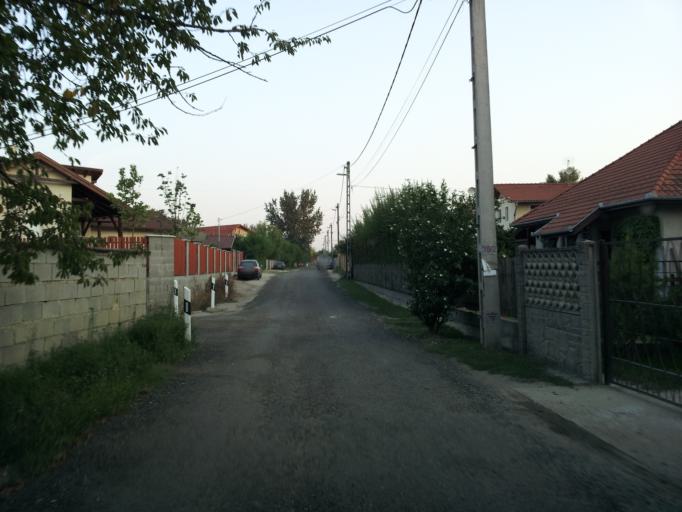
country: HU
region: Pest
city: Szigetszentmiklos
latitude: 47.3331
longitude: 19.0286
